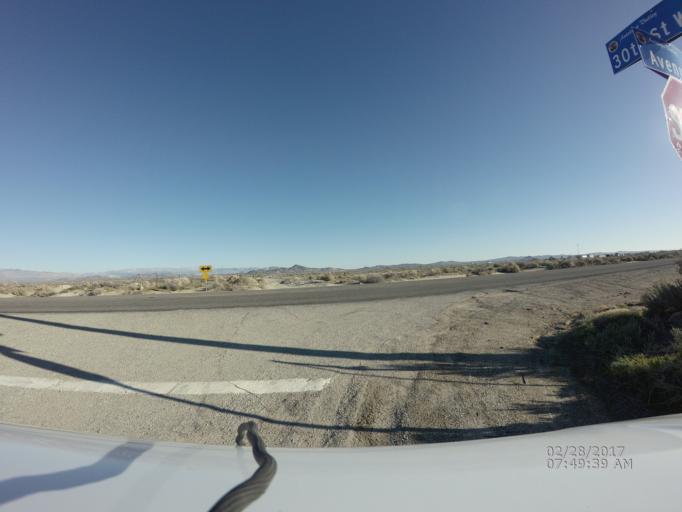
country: US
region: California
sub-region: Kern County
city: Rosamond
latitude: 34.8200
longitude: -118.1848
